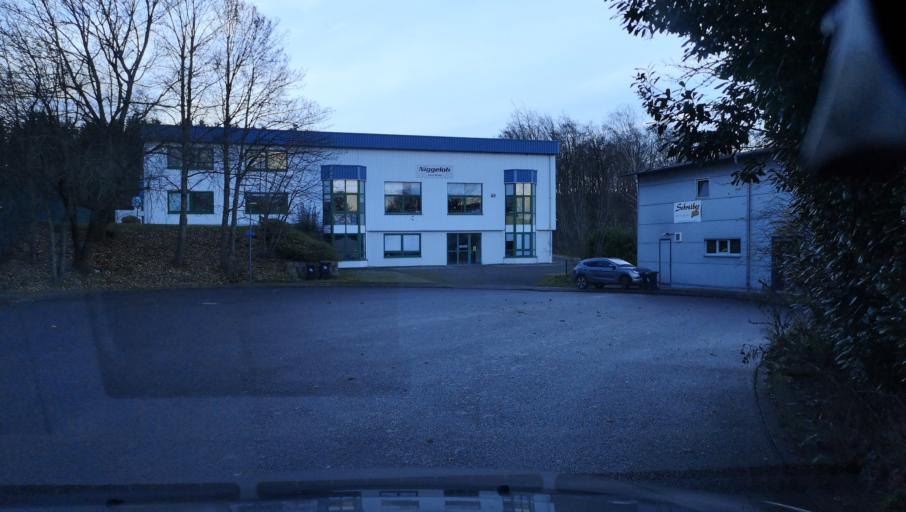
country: DE
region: North Rhine-Westphalia
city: Radevormwald
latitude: 51.2032
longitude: 7.3887
